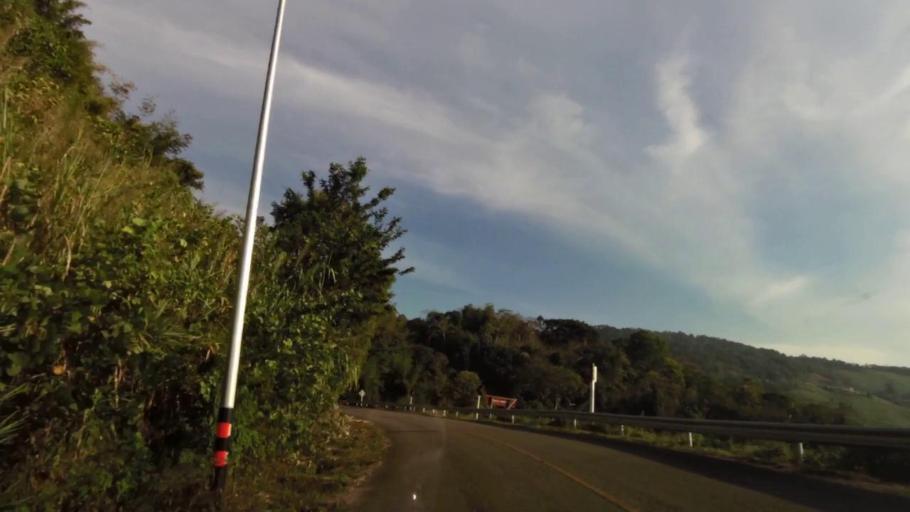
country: TH
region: Chiang Rai
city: Khun Tan
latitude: 19.8510
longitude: 100.4371
